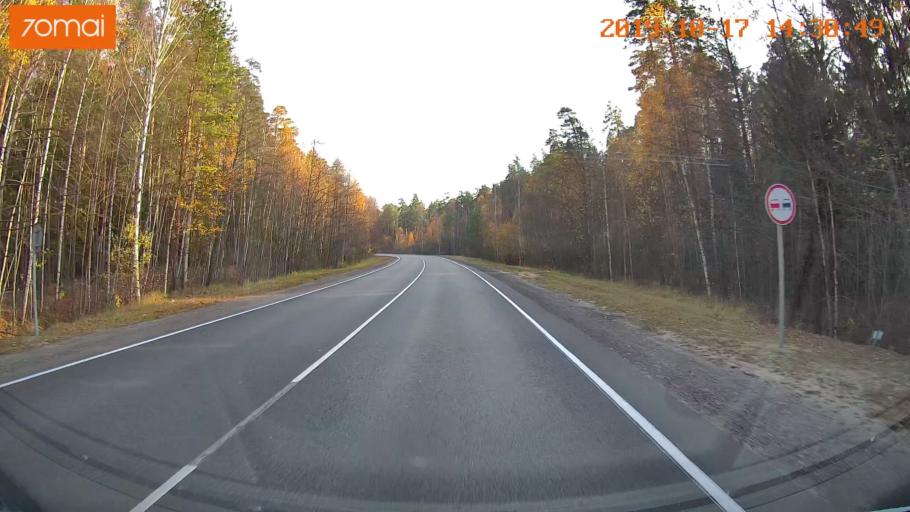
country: RU
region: Rjazan
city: Solotcha
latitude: 54.9427
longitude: 39.9506
